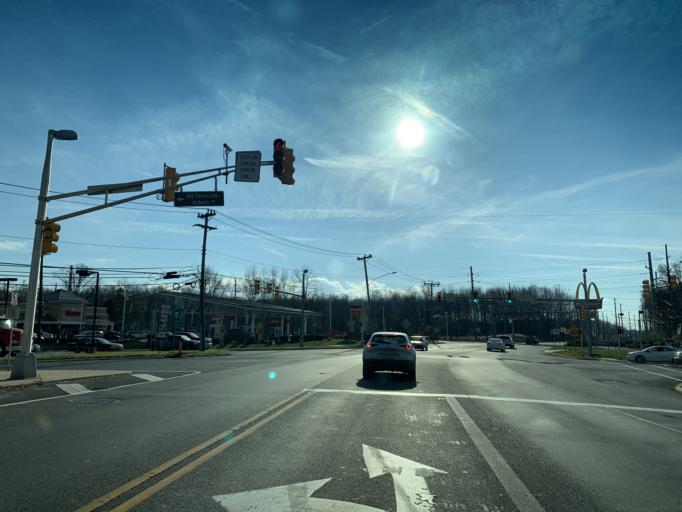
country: US
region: New Jersey
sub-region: Salem County
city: Pennsville
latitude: 39.6778
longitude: -75.4943
